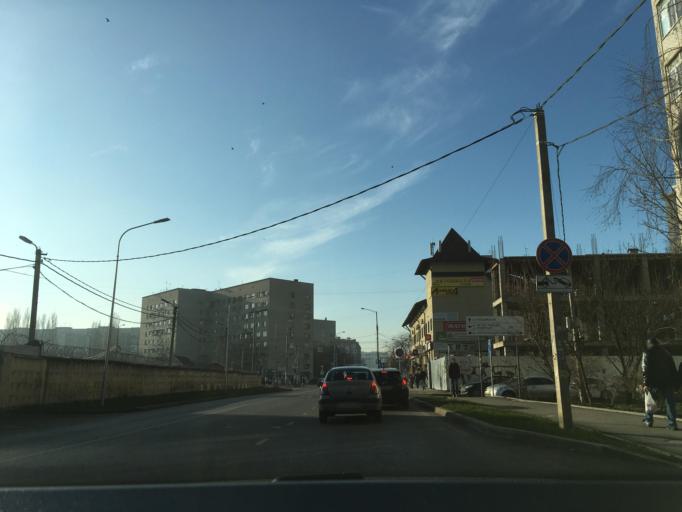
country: RU
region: Krasnodarskiy
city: Krasnodar
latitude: 45.0658
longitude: 39.0265
